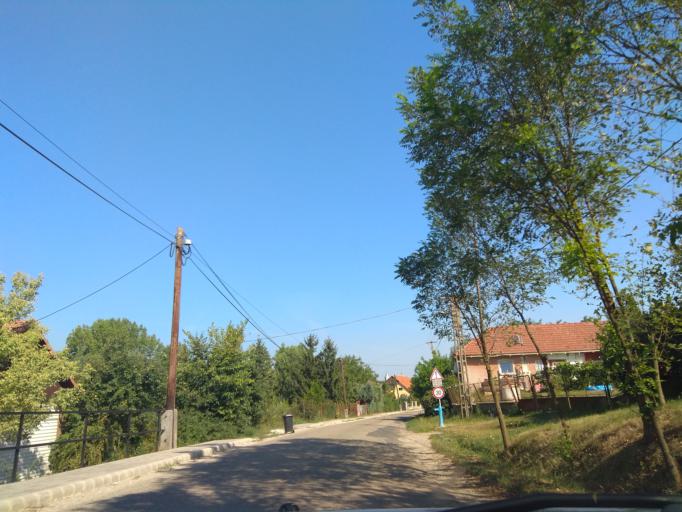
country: HU
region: Borsod-Abauj-Zemplen
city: Harsany
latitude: 47.9796
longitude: 20.7879
